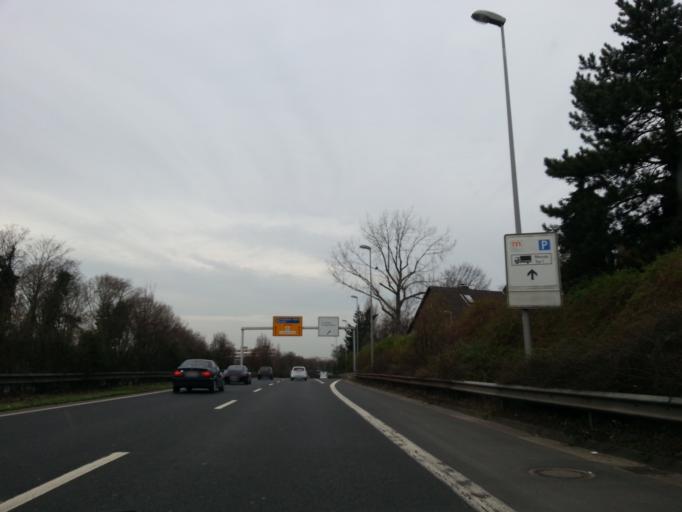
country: DE
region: North Rhine-Westphalia
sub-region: Regierungsbezirk Dusseldorf
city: Dusseldorf
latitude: 51.2640
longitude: 6.7575
